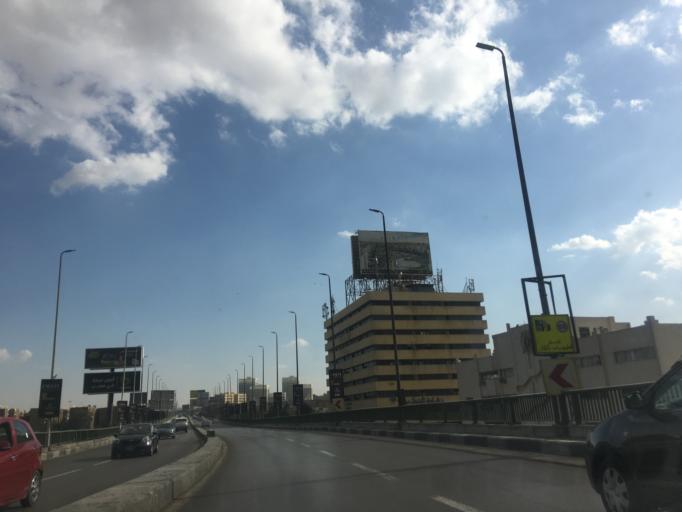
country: EG
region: Muhafazat al Qahirah
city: Cairo
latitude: 30.0676
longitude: 31.2930
